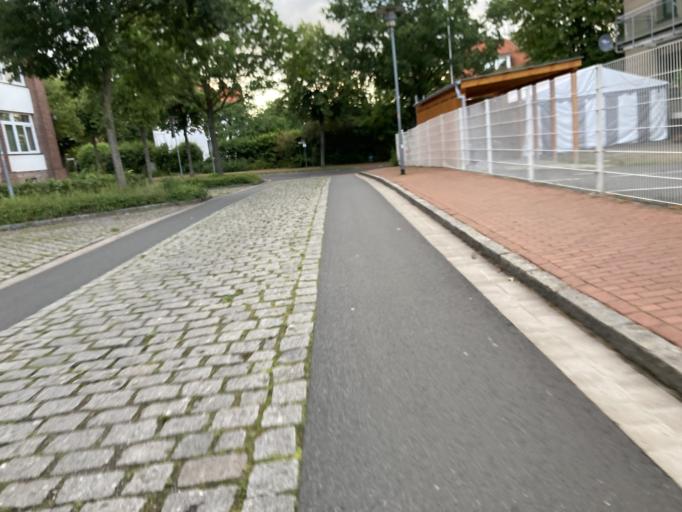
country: DE
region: Lower Saxony
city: Verden
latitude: 52.9156
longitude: 9.2384
